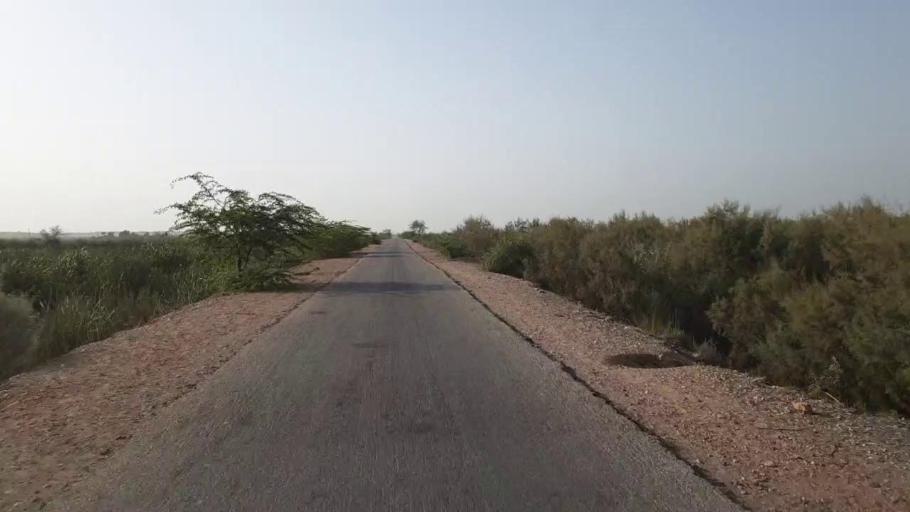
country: PK
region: Sindh
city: Jam Sahib
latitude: 26.4458
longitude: 68.8645
